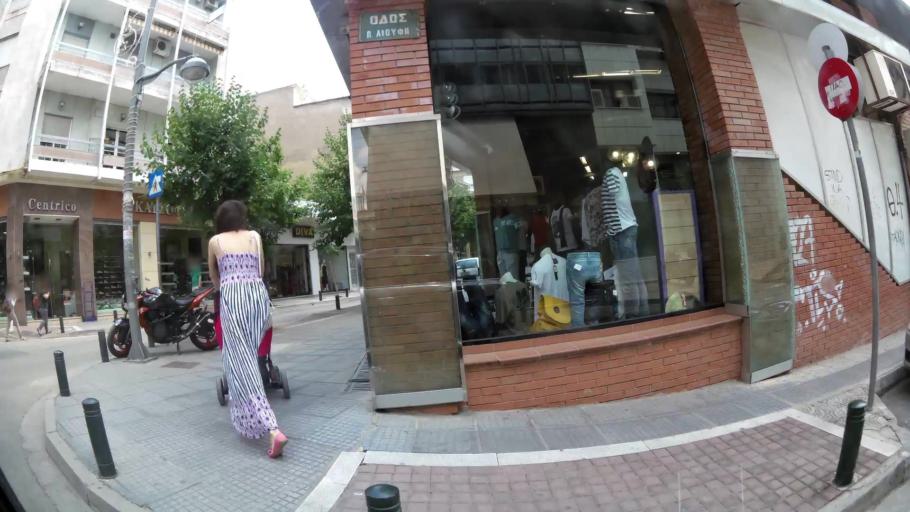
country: GR
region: West Macedonia
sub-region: Nomos Kozanis
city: Kozani
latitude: 40.3003
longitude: 21.7899
